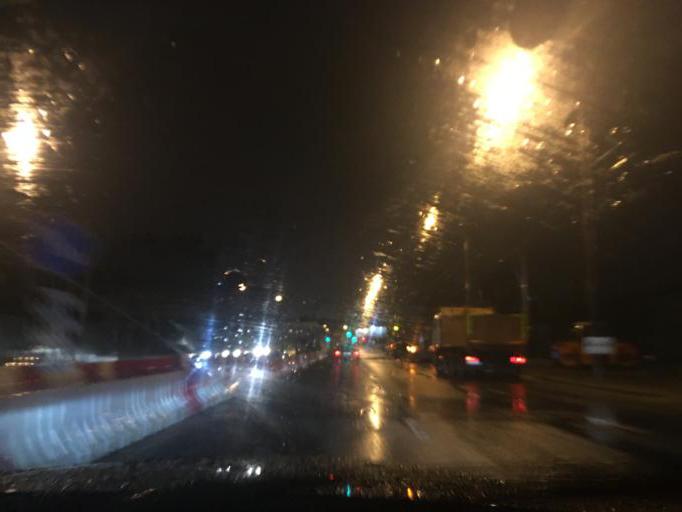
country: BY
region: Minsk
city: Minsk
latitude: 53.8942
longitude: 27.5322
